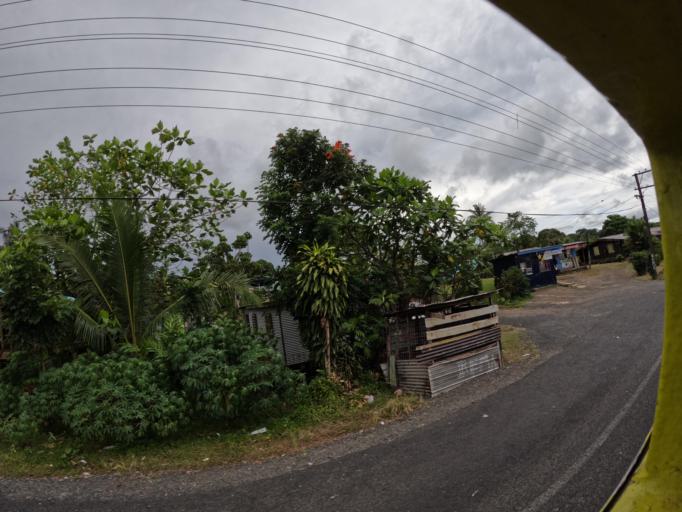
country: FJ
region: Central
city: Suva
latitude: -18.0754
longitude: 178.4600
